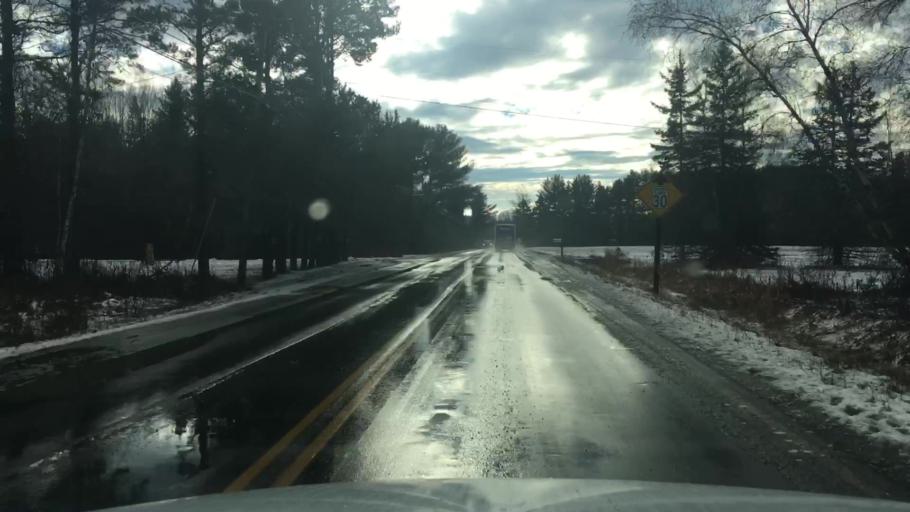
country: US
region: Maine
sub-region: Penobscot County
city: Brewer
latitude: 44.7451
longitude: -68.7662
